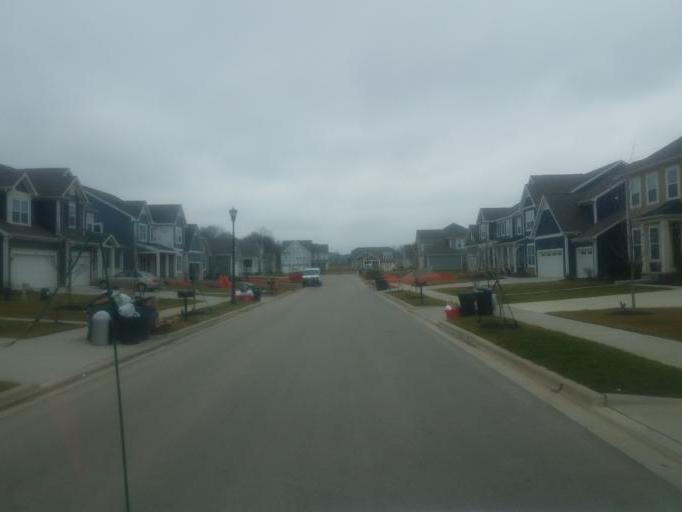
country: US
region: Ohio
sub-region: Franklin County
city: Westerville
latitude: 40.1310
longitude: -82.9571
